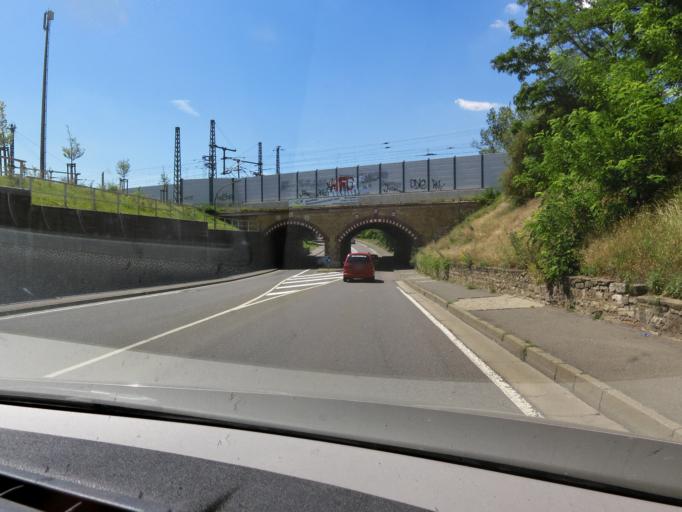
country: DE
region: Saxony-Anhalt
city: Merseburg
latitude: 51.3497
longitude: 11.9906
